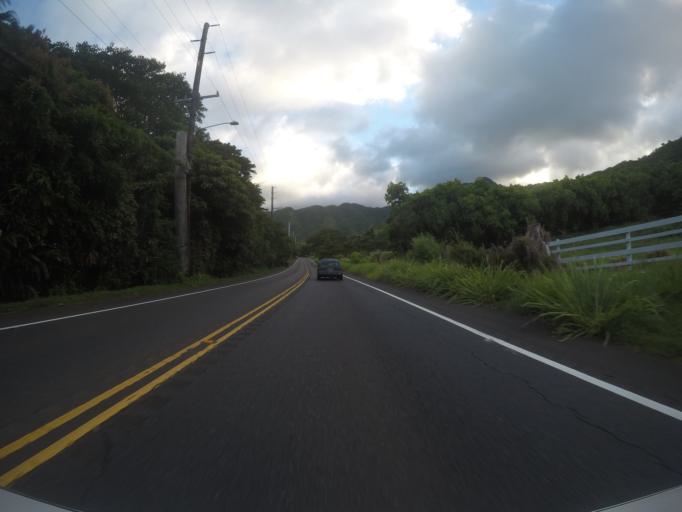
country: US
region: Hawaii
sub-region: Honolulu County
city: Ka'a'awa
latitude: 21.5126
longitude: -157.8496
